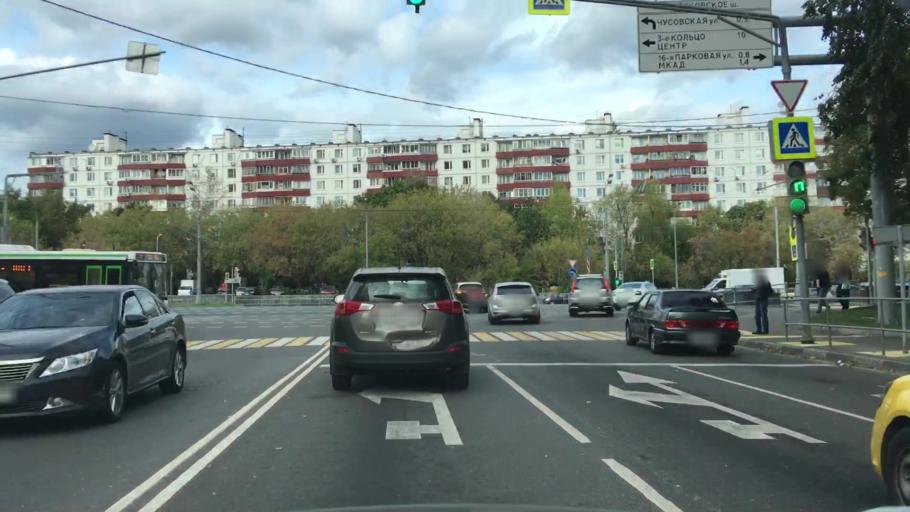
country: RU
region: Moscow
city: Gol'yanovo
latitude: 55.8107
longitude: 37.8169
